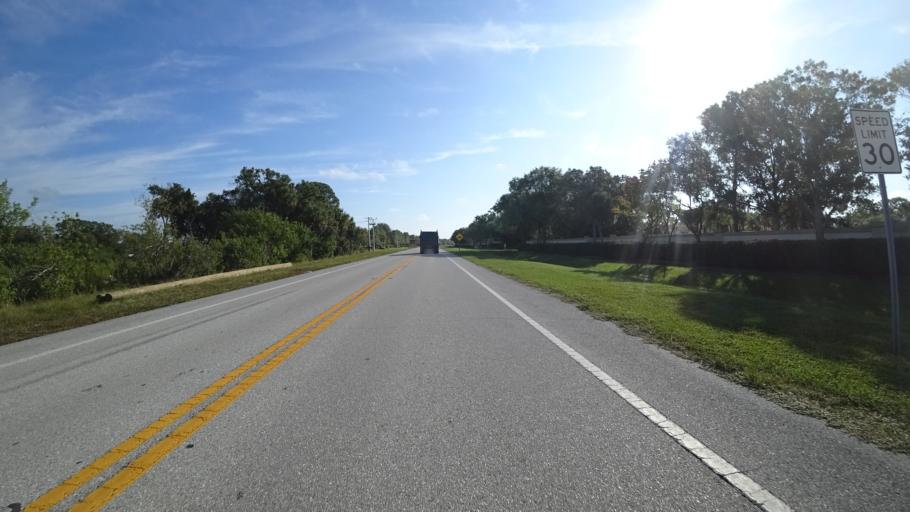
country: US
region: Florida
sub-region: Sarasota County
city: North Sarasota
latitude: 27.4185
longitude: -82.5022
